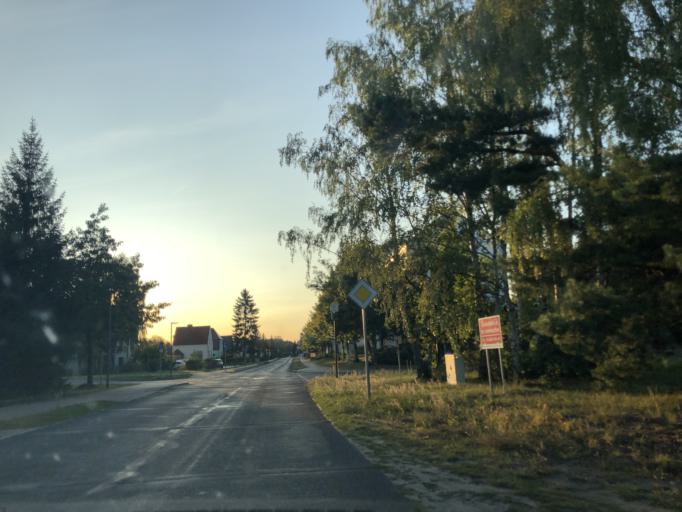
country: DE
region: Brandenburg
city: Mullrose
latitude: 52.2536
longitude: 14.4276
